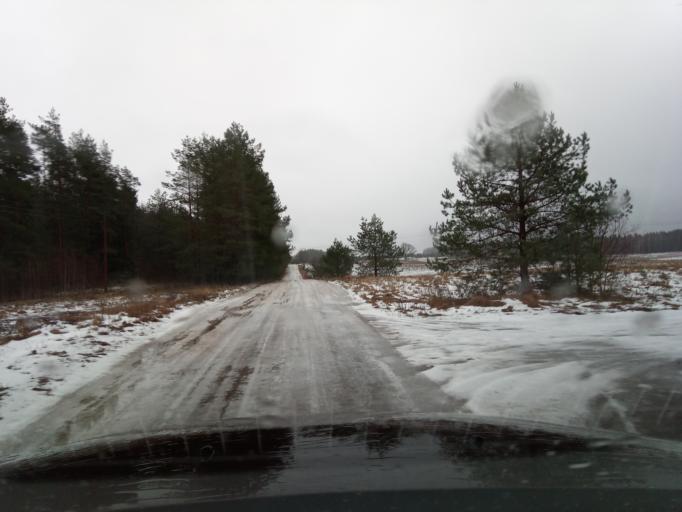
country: LT
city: Svencioneliai
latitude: 55.3460
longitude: 25.8330
